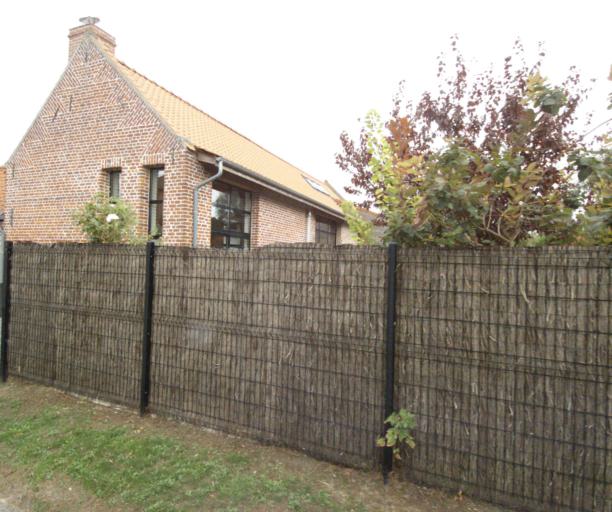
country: FR
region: Nord-Pas-de-Calais
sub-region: Departement du Nord
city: Sainghin-en-Melantois
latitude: 50.5663
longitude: 3.1670
